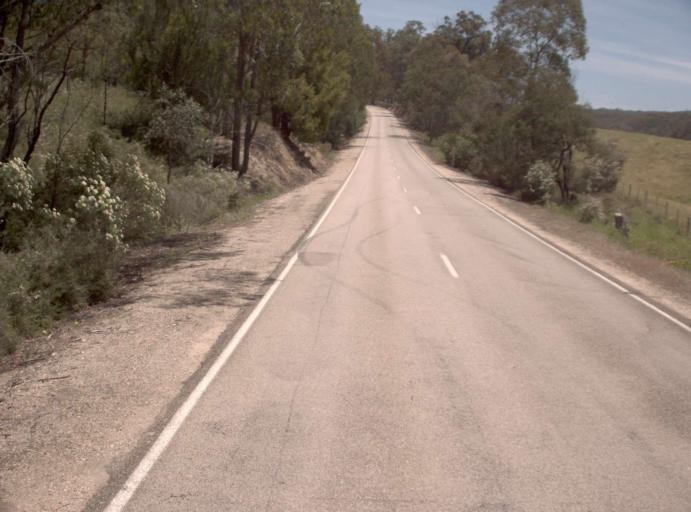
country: AU
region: Victoria
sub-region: East Gippsland
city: Lakes Entrance
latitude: -37.6727
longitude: 147.8622
